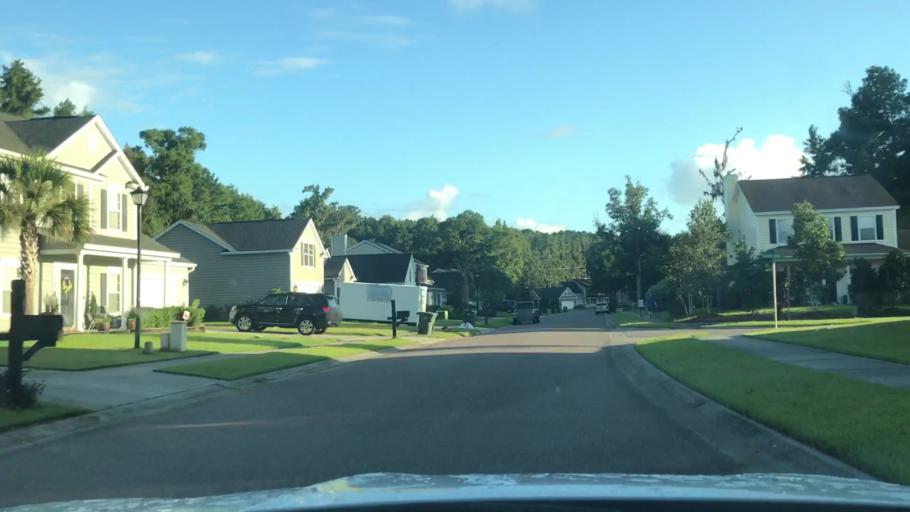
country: US
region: South Carolina
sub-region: Charleston County
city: Shell Point
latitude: 32.8355
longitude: -80.1018
